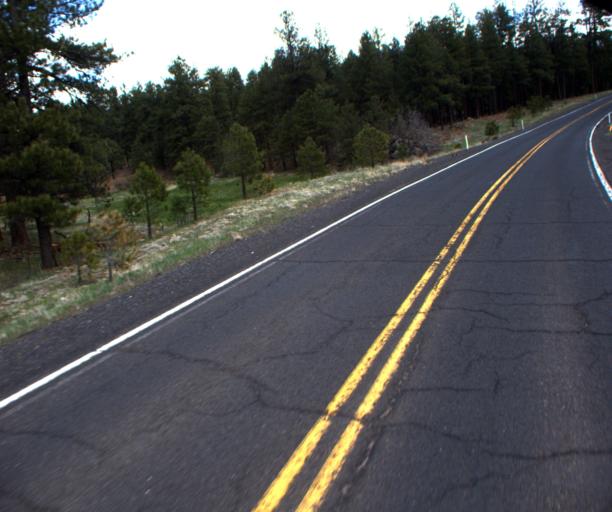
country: US
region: Arizona
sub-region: Coconino County
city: Kachina Village
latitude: 35.1200
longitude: -111.7081
